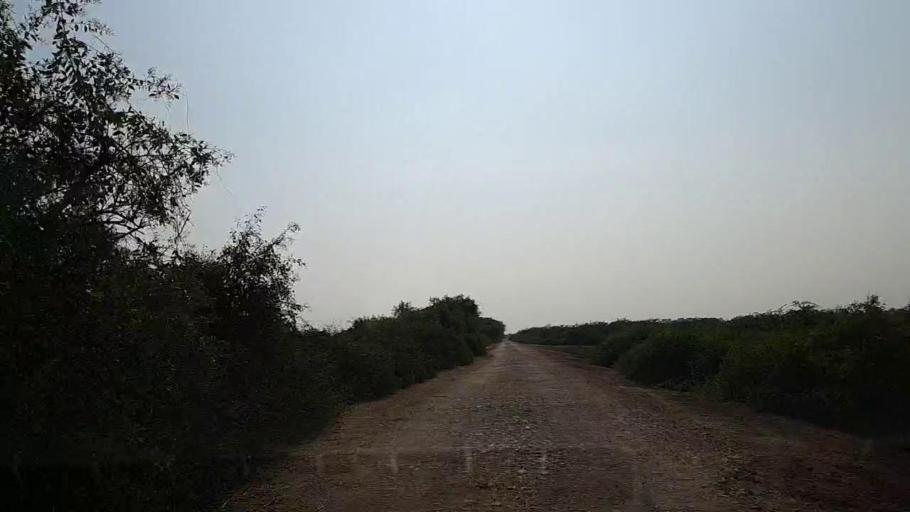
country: PK
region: Sindh
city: Mirpur Sakro
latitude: 24.6342
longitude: 67.6593
